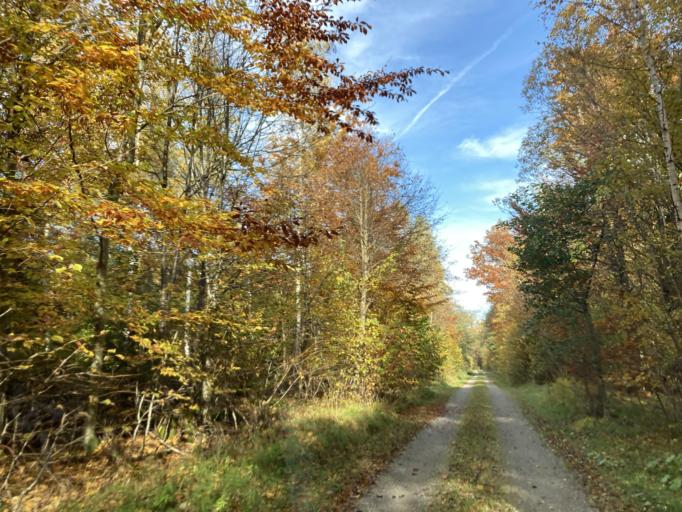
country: DE
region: Baden-Wuerttemberg
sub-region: Tuebingen Region
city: Bodelshausen
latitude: 48.4352
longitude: 8.9674
